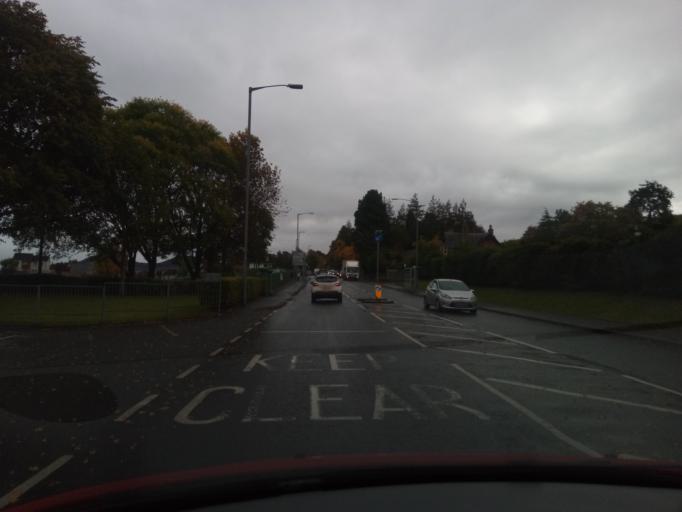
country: GB
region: Scotland
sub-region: The Scottish Borders
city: Galashiels
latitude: 55.6093
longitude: -2.7981
